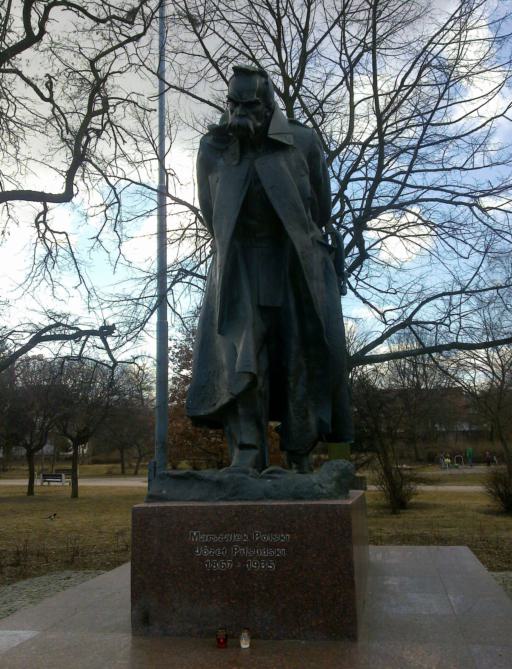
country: PL
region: Pomeranian Voivodeship
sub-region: Sopot
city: Sopot
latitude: 54.3867
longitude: 18.5915
